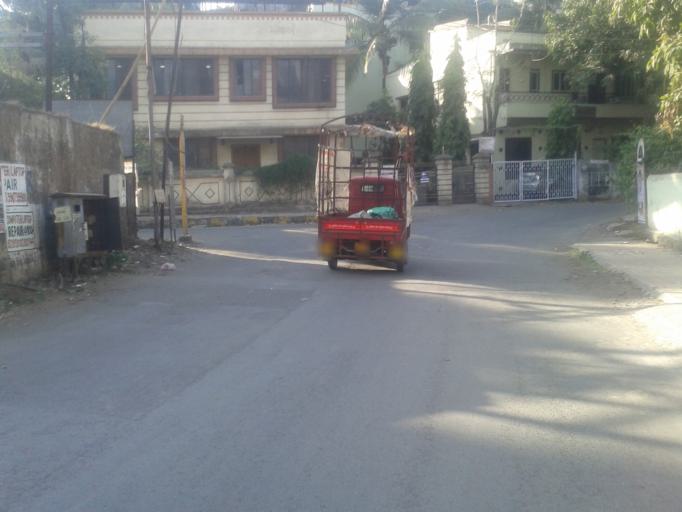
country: IN
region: Maharashtra
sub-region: Thane
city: Dombivli
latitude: 19.2061
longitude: 73.0898
